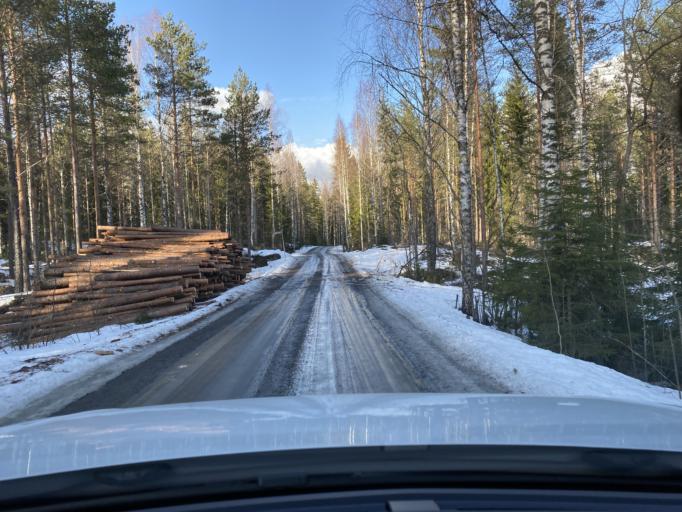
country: FI
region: Pirkanmaa
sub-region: Lounais-Pirkanmaa
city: Mouhijaervi
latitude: 61.4577
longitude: 22.9473
